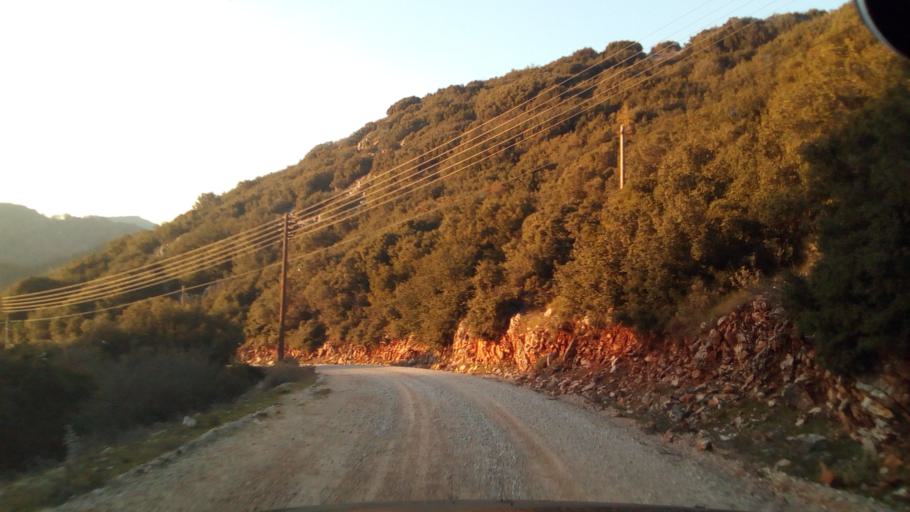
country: GR
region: West Greece
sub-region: Nomos Aitolias kai Akarnanias
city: Nafpaktos
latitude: 38.4684
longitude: 21.8226
